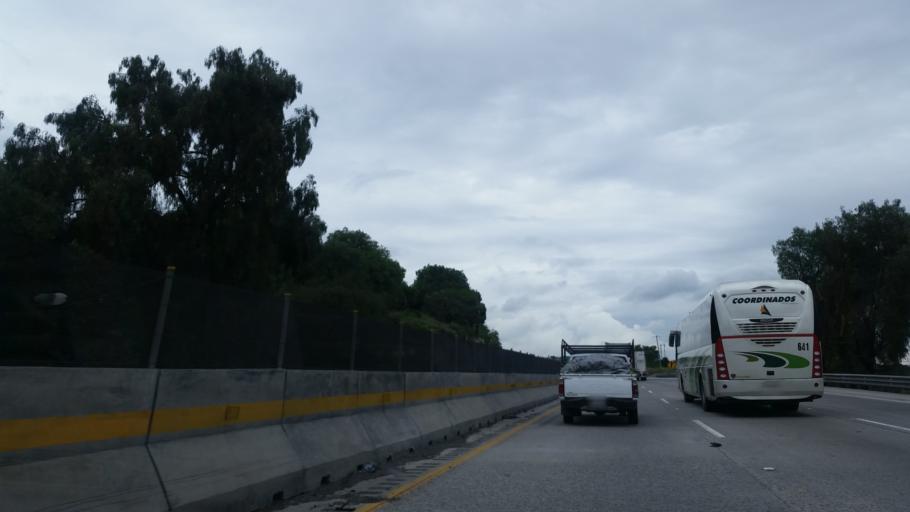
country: MX
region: Hidalgo
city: Tepeji de Ocampo
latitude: 19.8892
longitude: -99.3444
